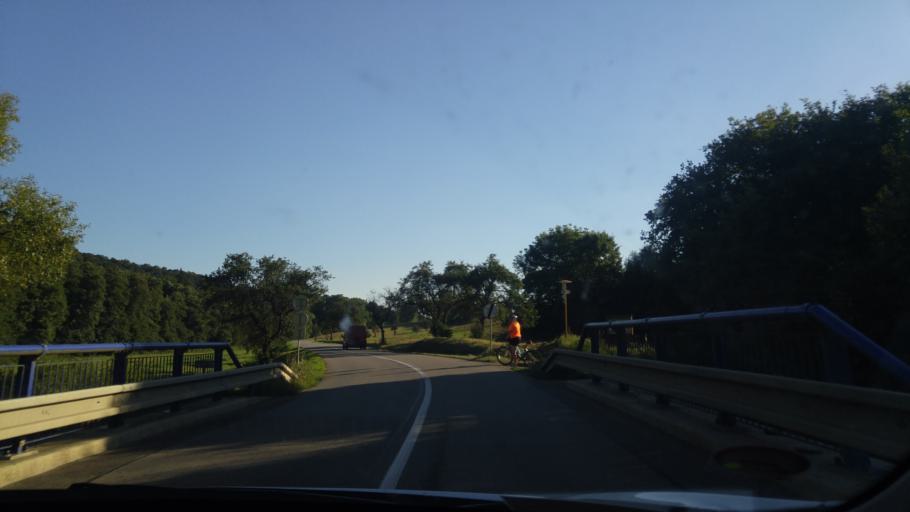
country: CZ
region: South Moravian
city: Veverska Bityska
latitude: 49.2450
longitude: 16.4460
